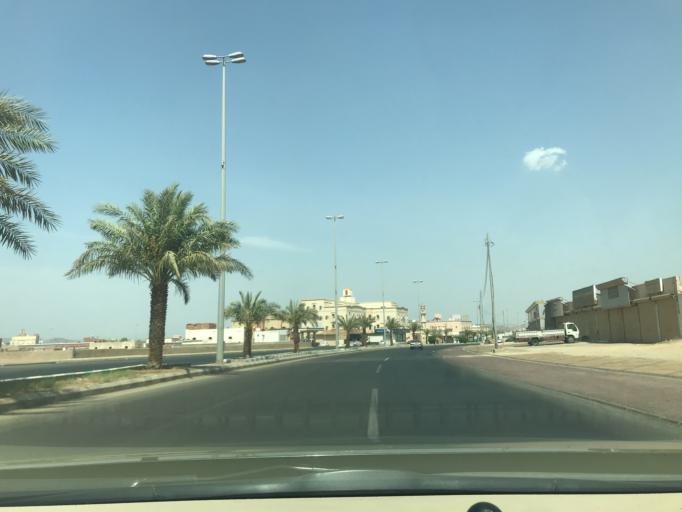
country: SA
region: Makkah
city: Al Jumum
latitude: 21.6247
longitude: 39.6774
